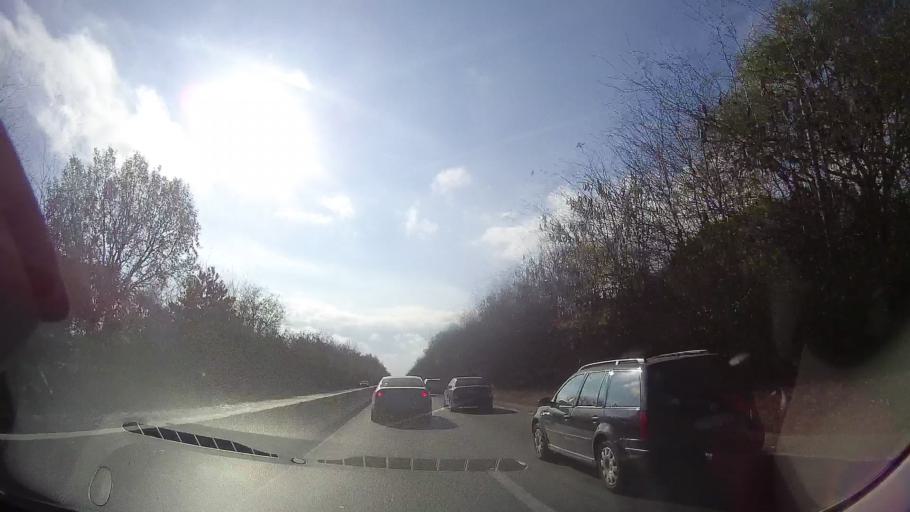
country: RO
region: Constanta
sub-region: Comuna Agigea
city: Agigea
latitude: 44.1298
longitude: 28.6167
